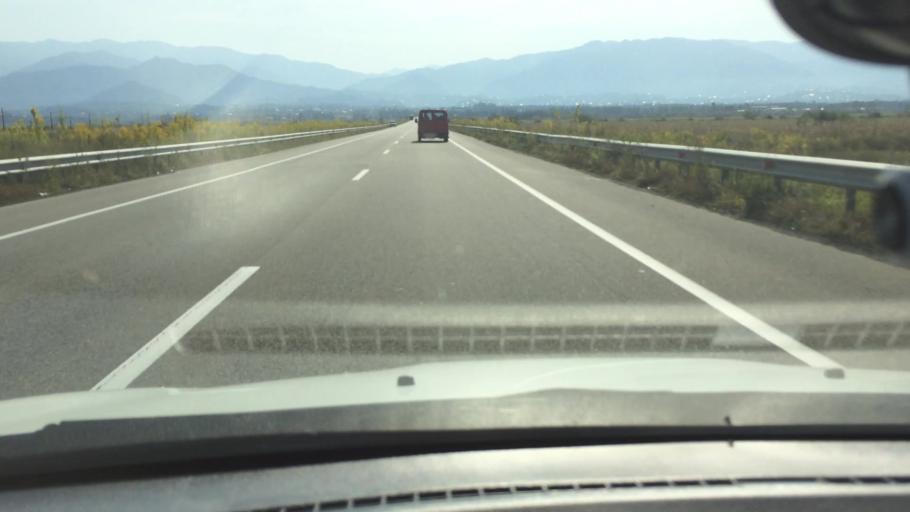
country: GE
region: Ajaria
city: Ochkhamuri
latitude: 41.8760
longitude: 41.8248
